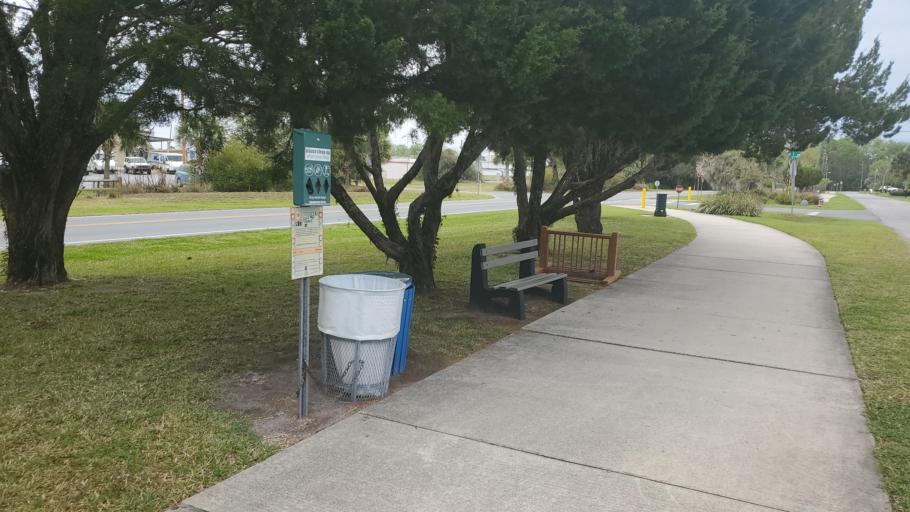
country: US
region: Florida
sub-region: Citrus County
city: Crystal River
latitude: 28.8950
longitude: -82.5890
